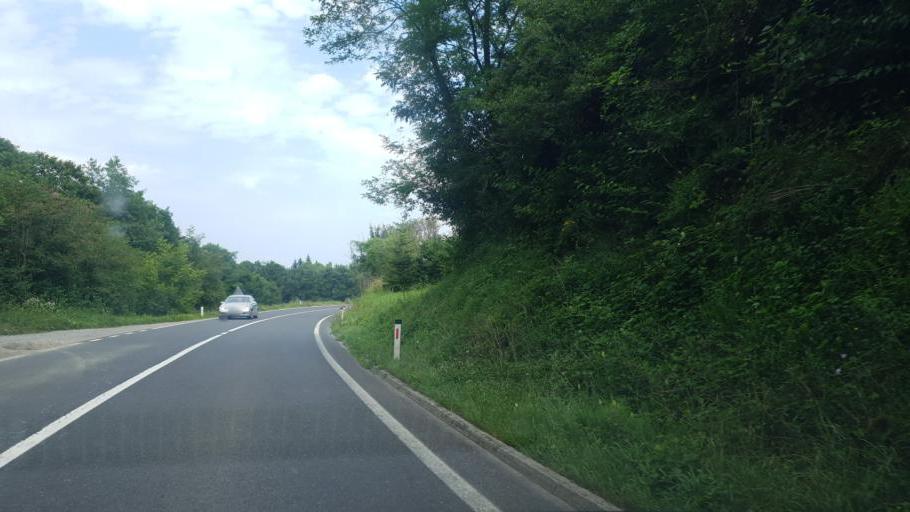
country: SI
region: Ilirska Bistrica
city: Ilirska Bistrica
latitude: 45.5364
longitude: 14.2495
